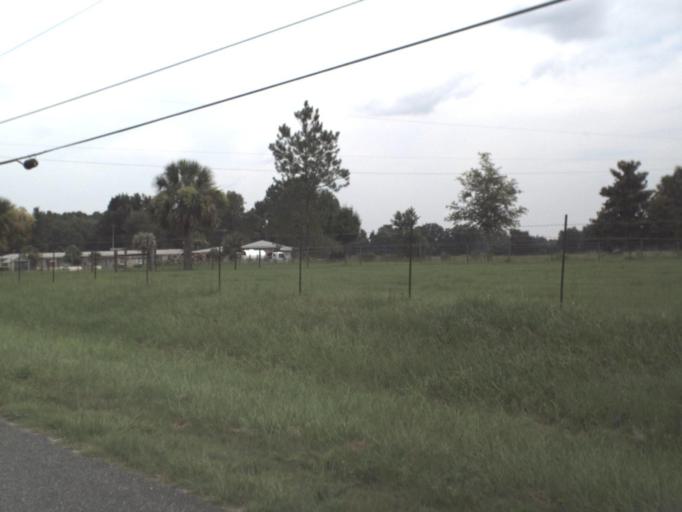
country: US
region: Florida
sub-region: Columbia County
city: Watertown
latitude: 30.1190
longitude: -82.6176
